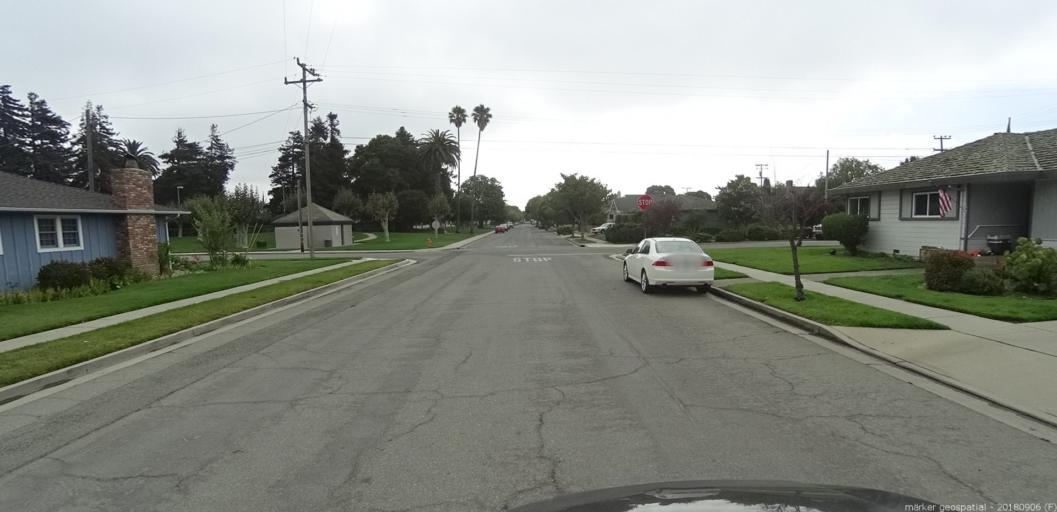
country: US
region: California
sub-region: Monterey County
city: Salinas
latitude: 36.6248
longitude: -121.6486
